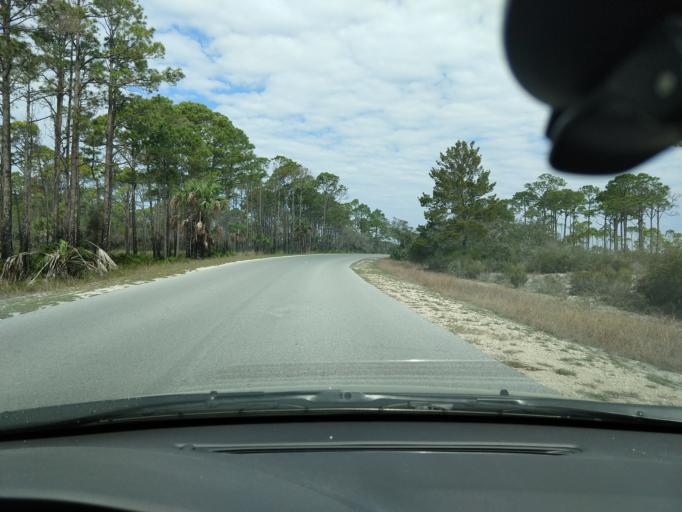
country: US
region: Florida
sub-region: Gulf County
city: Port Saint Joe
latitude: 29.7607
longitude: -85.3968
